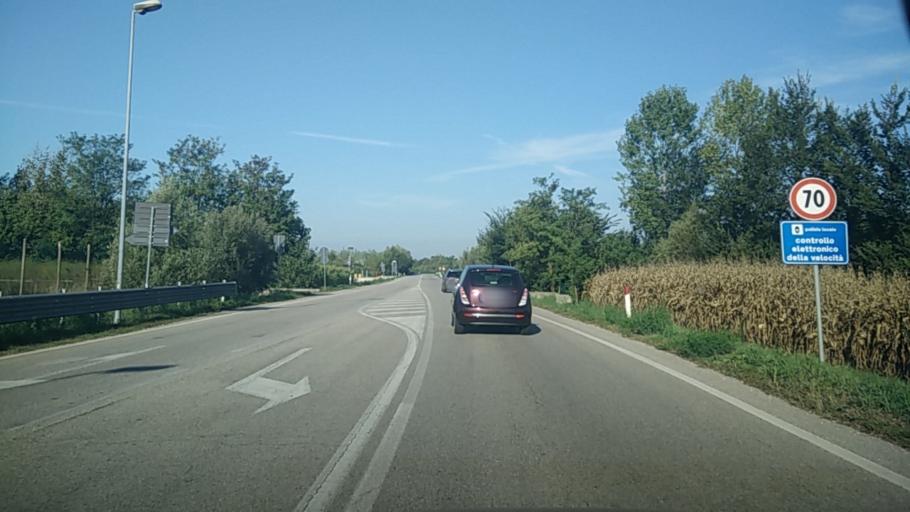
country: IT
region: Veneto
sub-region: Provincia di Padova
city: Piombino Dese
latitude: 45.6154
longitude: 11.9977
